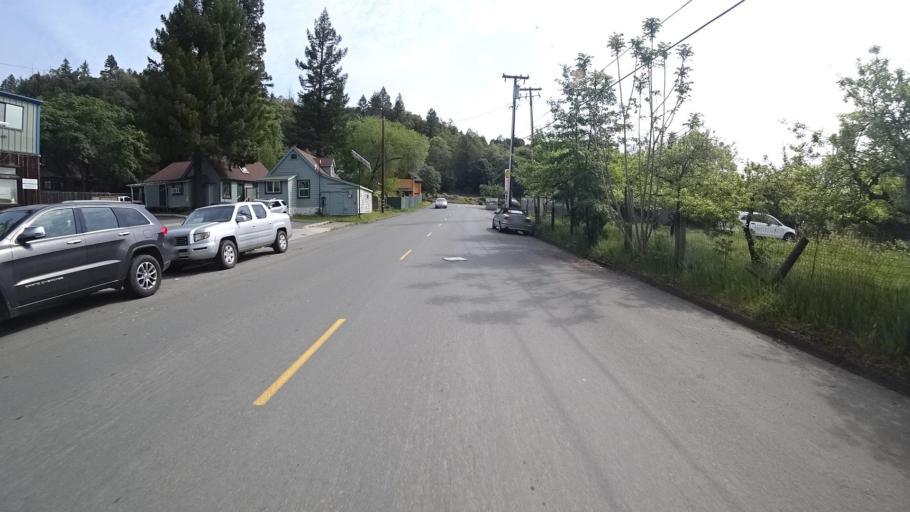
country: US
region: California
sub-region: Humboldt County
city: Redway
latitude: 40.1170
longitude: -123.8205
